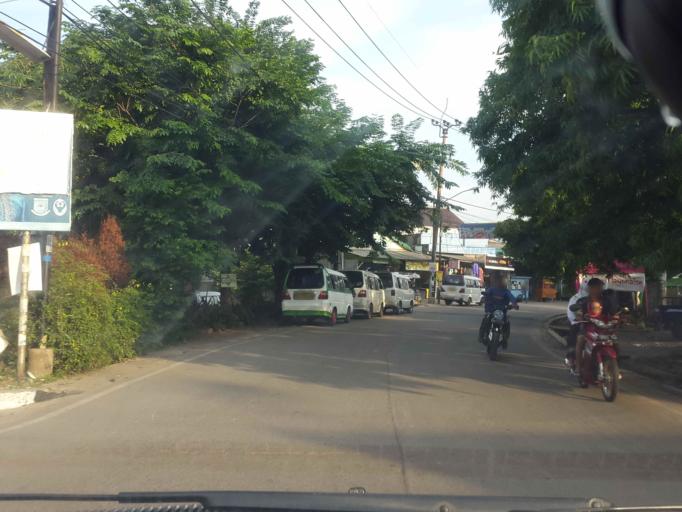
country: ID
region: West Java
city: Ciputat
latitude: -6.2605
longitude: 106.7101
